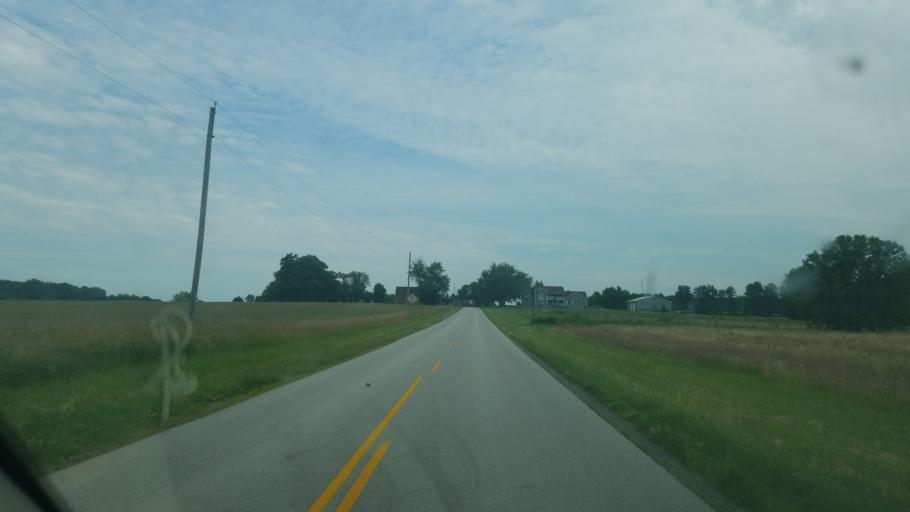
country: US
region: Ohio
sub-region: Wyandot County
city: Carey
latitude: 41.0327
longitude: -83.4398
